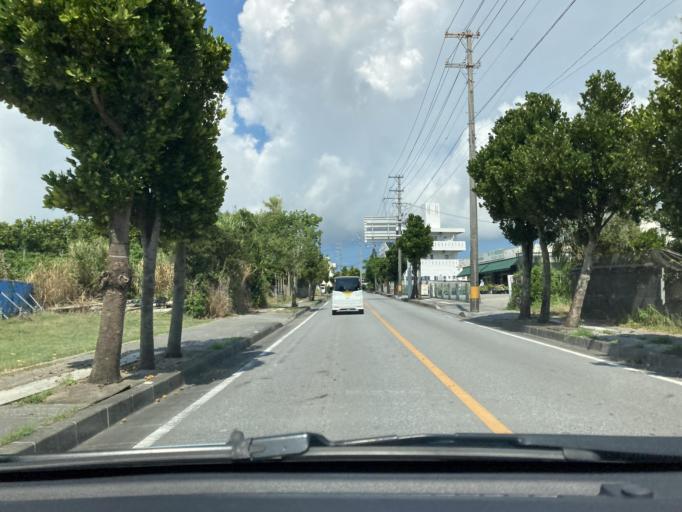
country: JP
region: Okinawa
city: Tomigusuku
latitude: 26.1707
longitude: 127.7379
